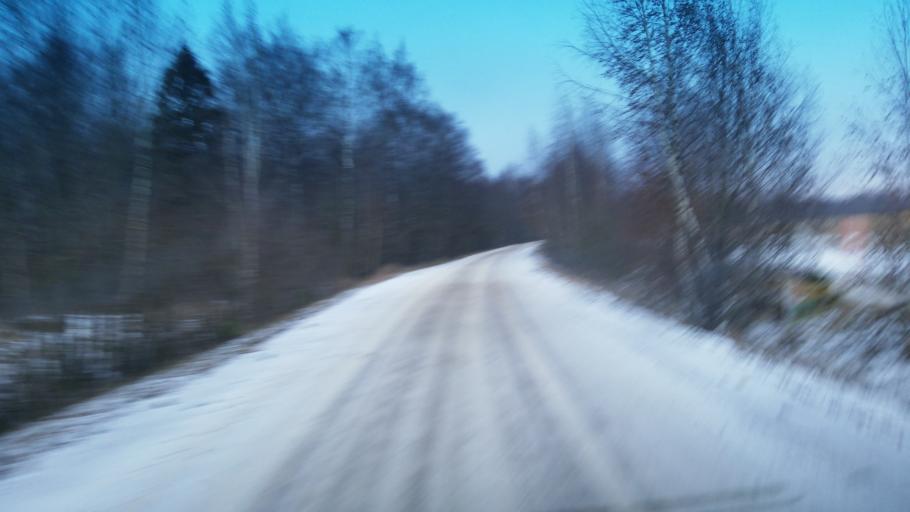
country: RU
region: Kostroma
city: Krasnoye-na-Volge
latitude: 57.6885
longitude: 41.1825
